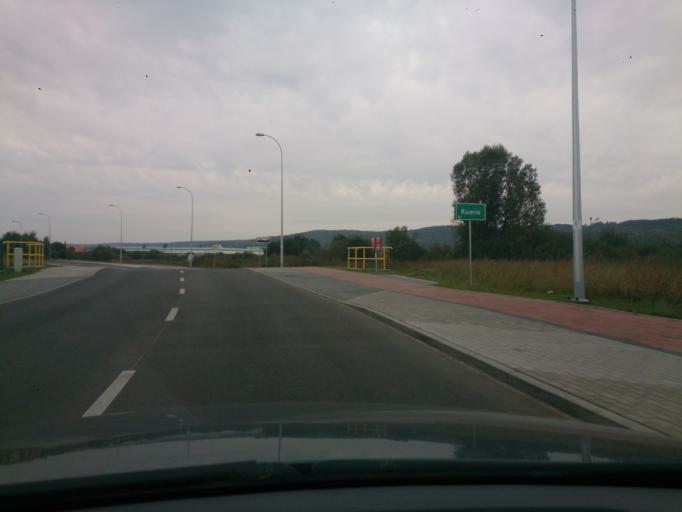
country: PL
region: Pomeranian Voivodeship
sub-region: Powiat wejherowski
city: Reda
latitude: 54.5916
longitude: 18.3675
